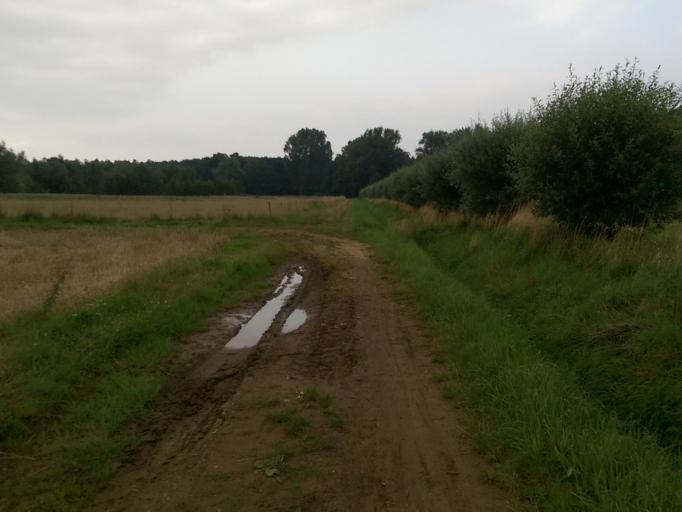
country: DE
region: North Rhine-Westphalia
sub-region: Regierungsbezirk Detmold
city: Rheda-Wiedenbruck
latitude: 51.8905
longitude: 8.3176
